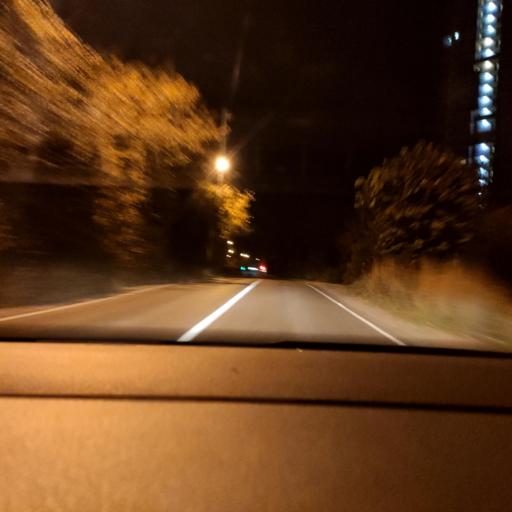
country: RU
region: Moskovskaya
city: Bolshevo
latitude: 55.9463
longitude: 37.8316
